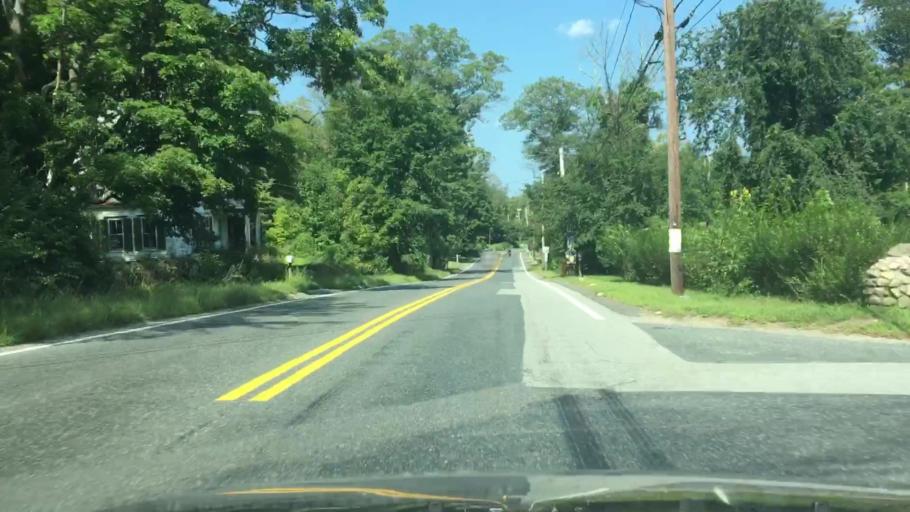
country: US
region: Massachusetts
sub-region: Worcester County
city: Milford
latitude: 42.1663
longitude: -71.4797
